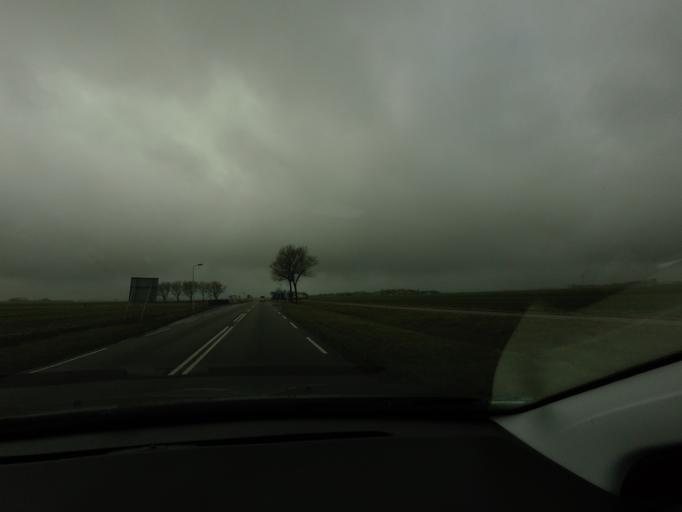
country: NL
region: Friesland
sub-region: Sudwest Fryslan
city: Makkum
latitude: 53.0875
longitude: 5.4407
